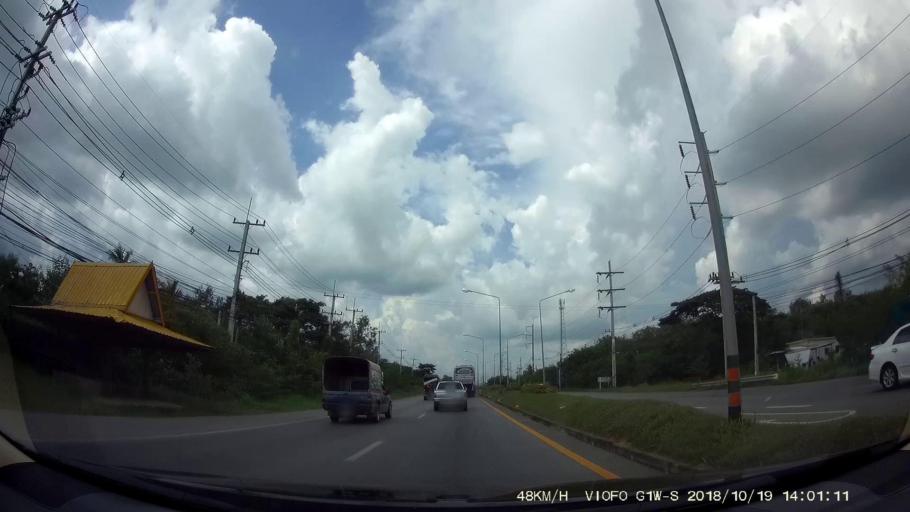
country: TH
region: Chaiyaphum
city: Chaiyaphum
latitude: 15.8269
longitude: 102.0590
